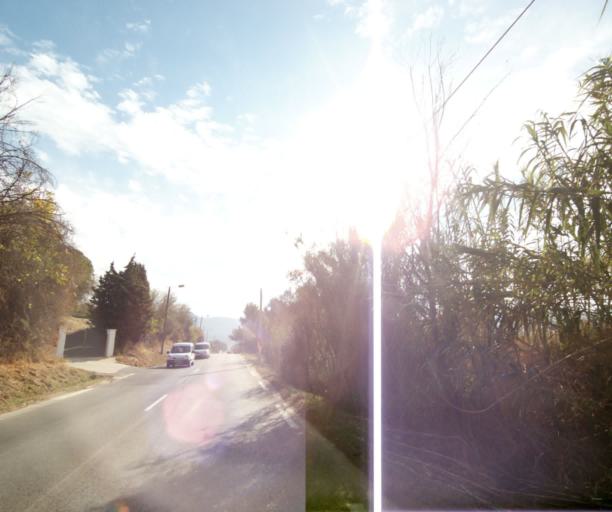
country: FR
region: Provence-Alpes-Cote d'Azur
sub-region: Departement des Bouches-du-Rhone
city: Gemenos
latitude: 43.3072
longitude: 5.6102
